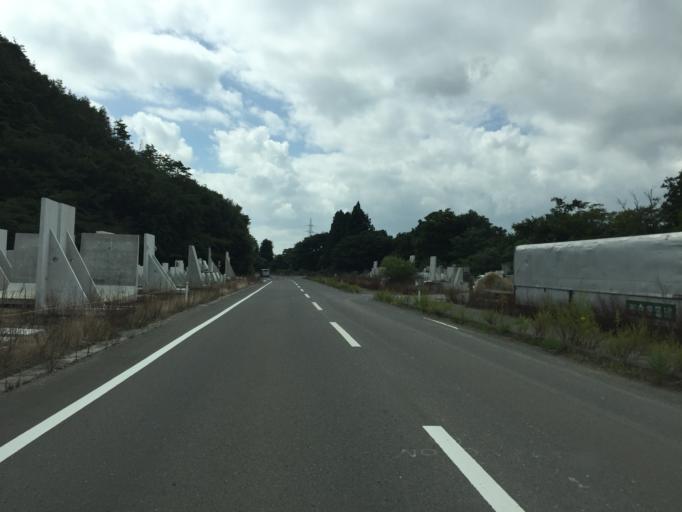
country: JP
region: Fukushima
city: Motomiya
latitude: 37.4785
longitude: 140.3371
